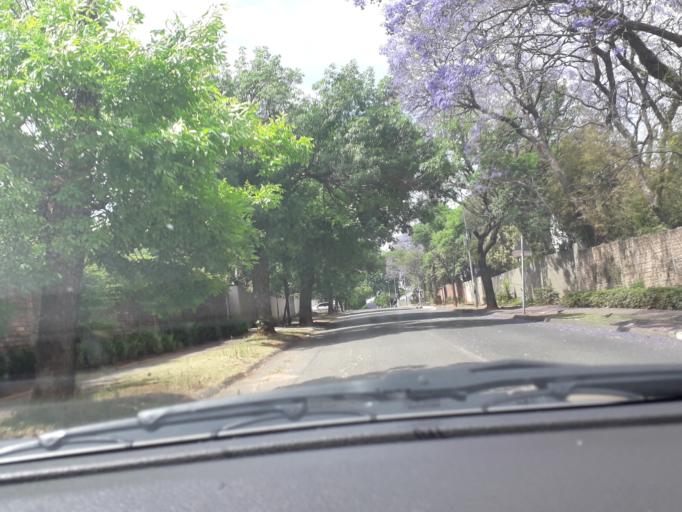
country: ZA
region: Gauteng
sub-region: City of Johannesburg Metropolitan Municipality
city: Johannesburg
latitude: -26.1237
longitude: 28.0765
